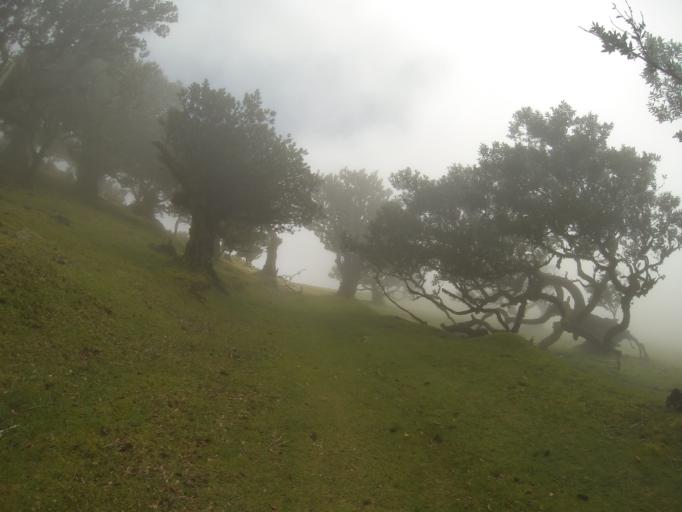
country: PT
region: Madeira
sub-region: Porto Moniz
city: Porto Moniz
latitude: 32.8142
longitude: -17.1446
